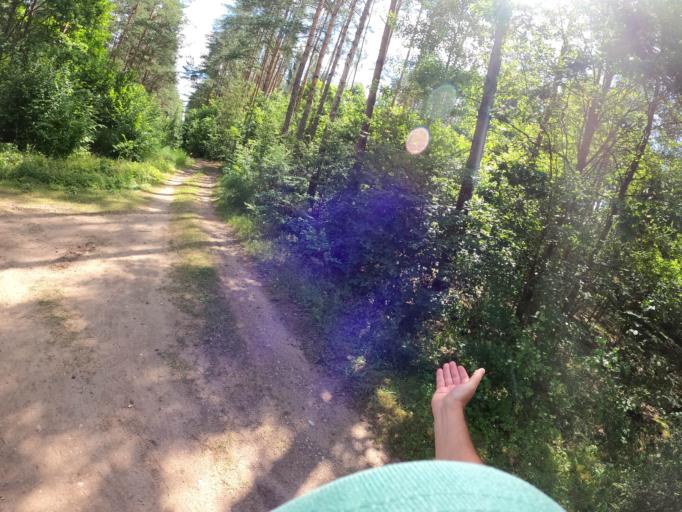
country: LT
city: Birstonas
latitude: 54.6529
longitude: 24.0908
